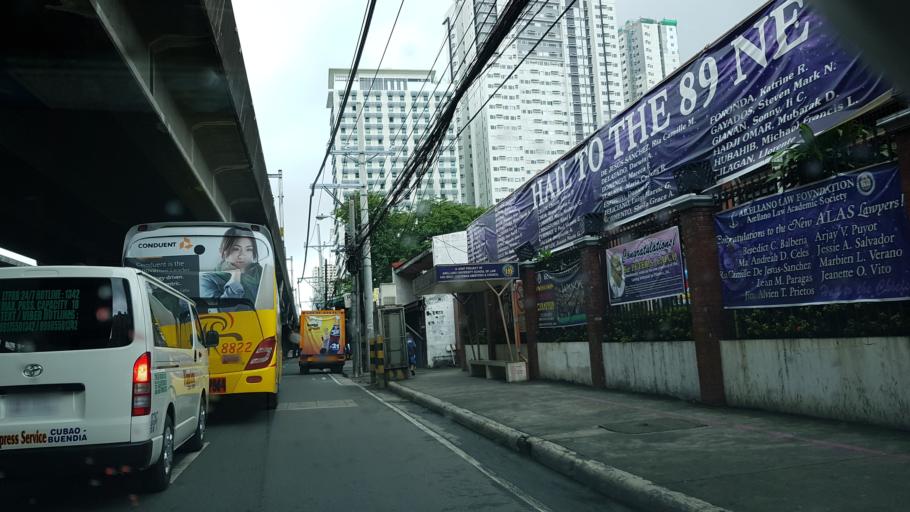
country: PH
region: Metro Manila
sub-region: City of Manila
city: Port Area
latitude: 14.5602
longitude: 120.9959
